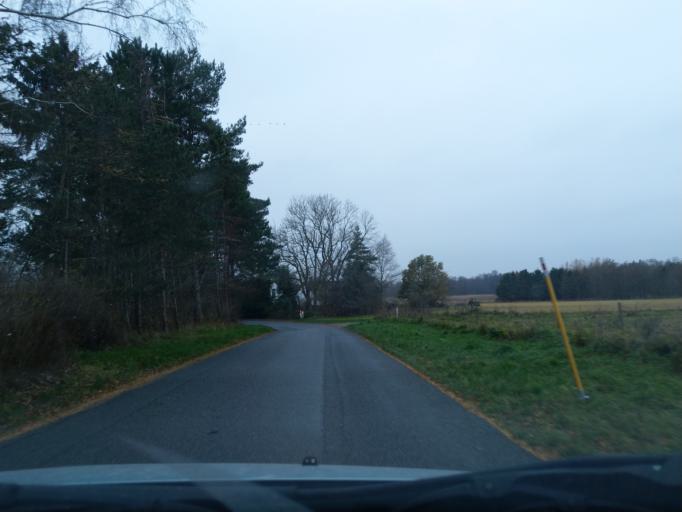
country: DK
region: Zealand
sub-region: Vordingborg Kommune
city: Praesto
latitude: 55.1187
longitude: 12.1204
